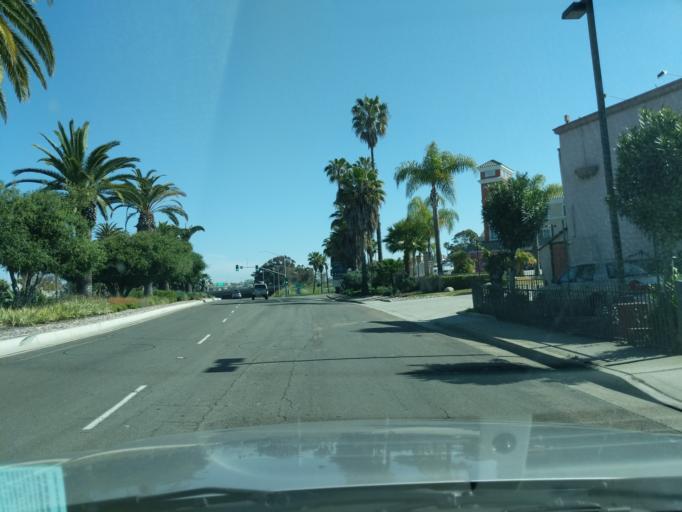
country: US
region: California
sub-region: San Diego County
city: Oceanside
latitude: 33.2019
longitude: -117.3837
